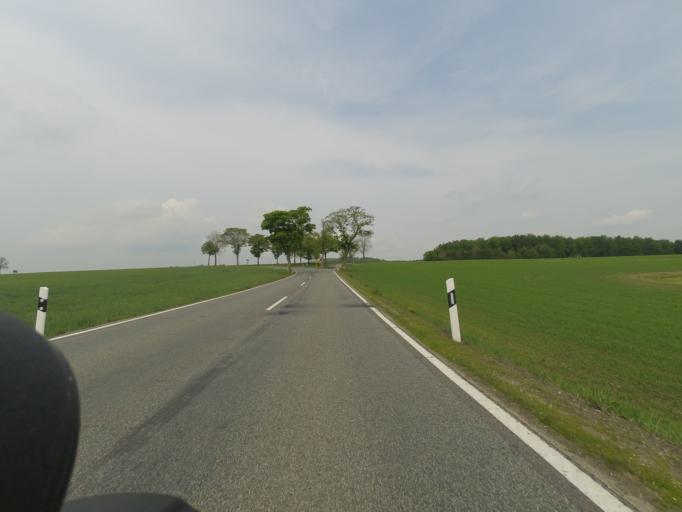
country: DE
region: Saxony
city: Zoblitz
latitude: 50.6499
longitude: 13.2796
